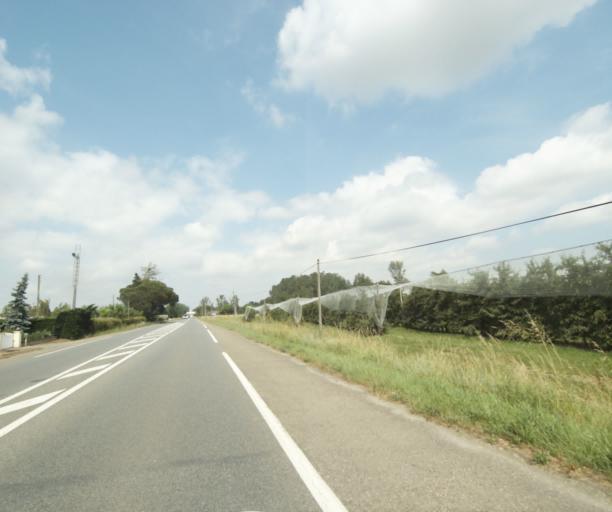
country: FR
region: Midi-Pyrenees
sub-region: Departement du Tarn-et-Garonne
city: Albias
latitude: 44.0658
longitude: 1.4162
